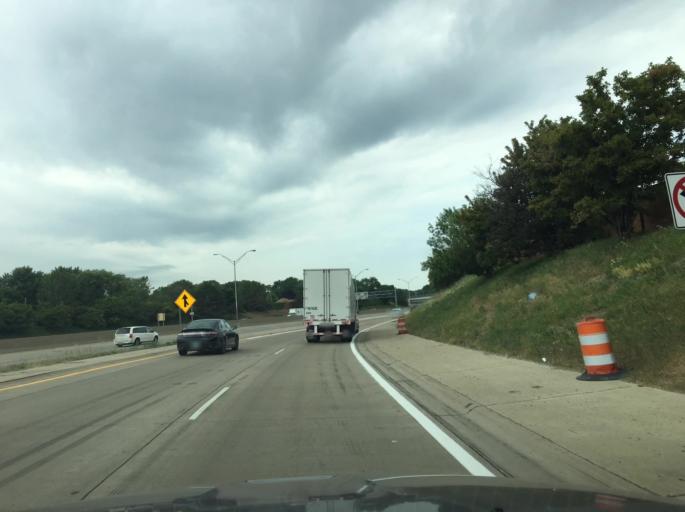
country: US
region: Michigan
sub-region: Macomb County
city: Center Line
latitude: 42.4890
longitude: -83.0507
